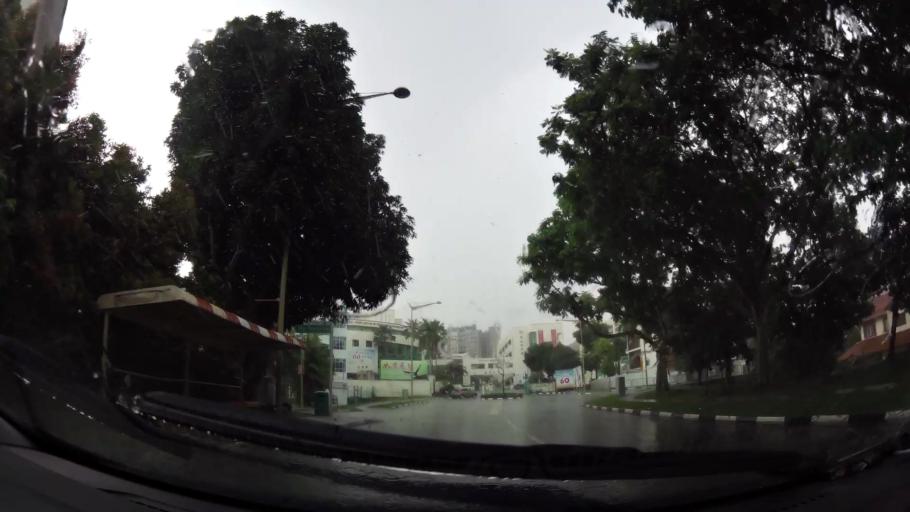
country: SG
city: Singapore
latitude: 1.3304
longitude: 103.9430
